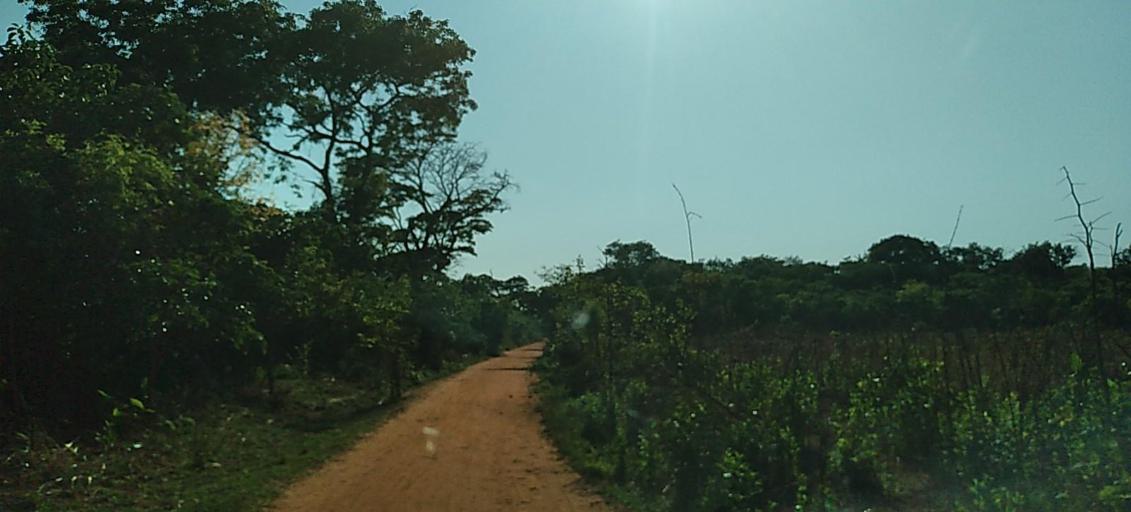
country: ZM
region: Copperbelt
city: Luanshya
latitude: -13.4590
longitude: 28.8219
